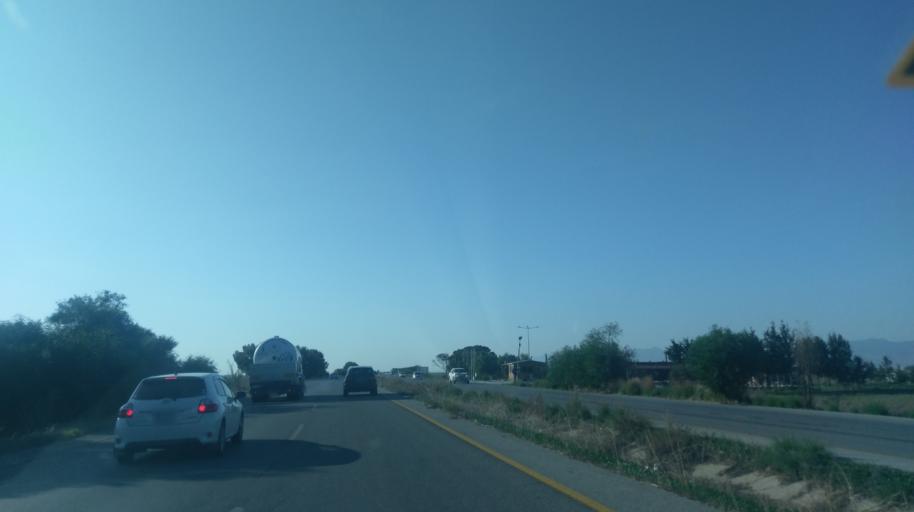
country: CY
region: Ammochostos
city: Lefkonoiko
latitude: 35.1803
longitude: 33.7224
